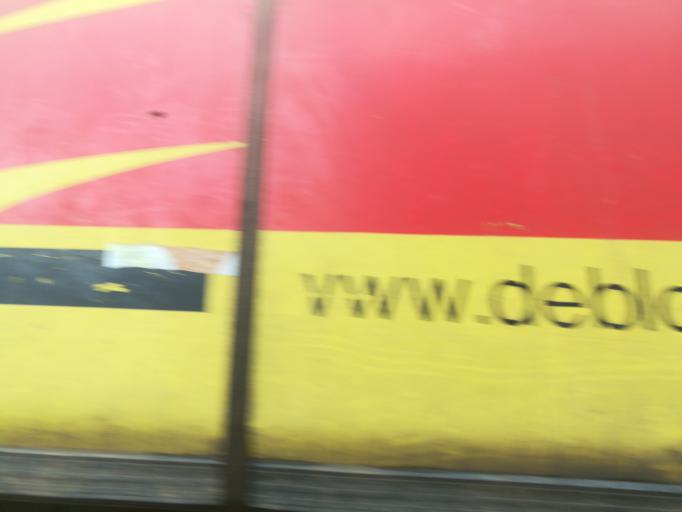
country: NG
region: Lagos
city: Agege
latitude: 6.6141
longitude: 3.3298
